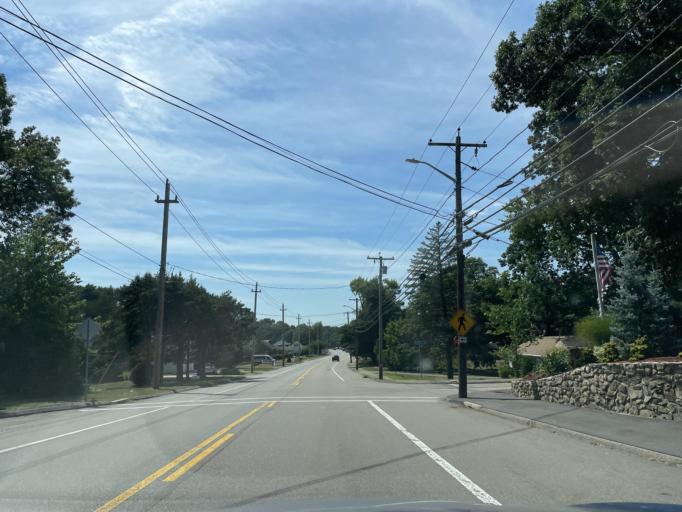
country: US
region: Massachusetts
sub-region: Norfolk County
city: Foxborough
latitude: 42.0761
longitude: -71.2729
